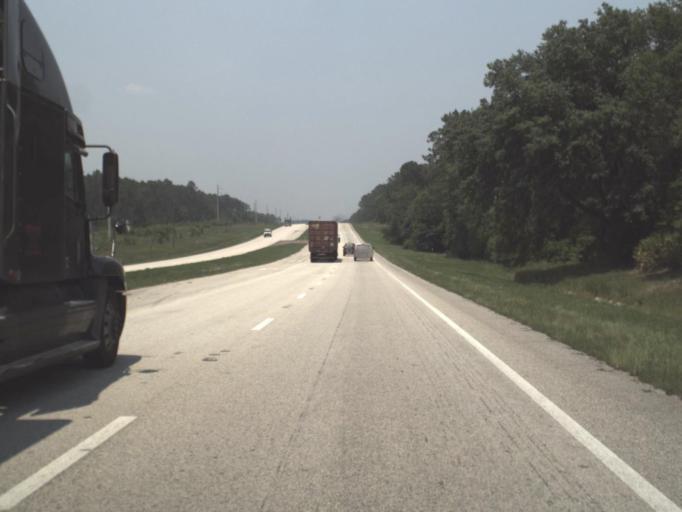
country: US
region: Florida
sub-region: Baker County
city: Macclenny
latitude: 30.1257
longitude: -82.0425
